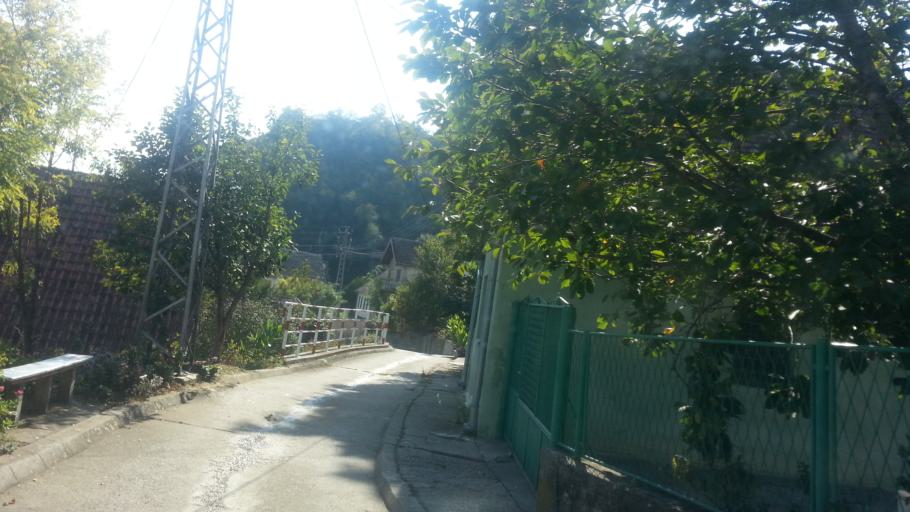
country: RS
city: Novi Slankamen
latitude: 45.1449
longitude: 20.2551
